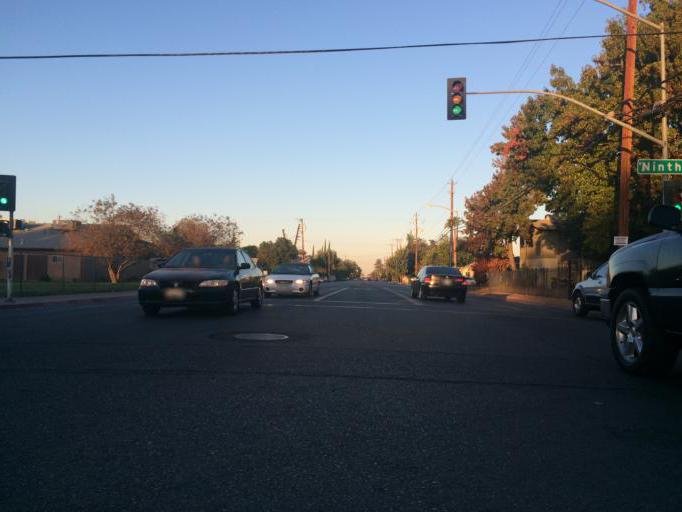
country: US
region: California
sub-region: Fresno County
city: Fresno
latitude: 36.7577
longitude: -119.7589
